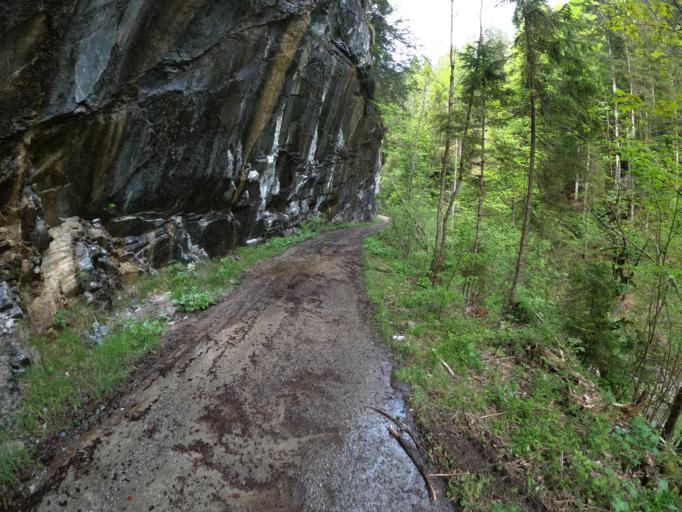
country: AT
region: Salzburg
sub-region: Politischer Bezirk Sankt Johann im Pongau
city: Werfen
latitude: 47.4820
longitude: 13.1567
